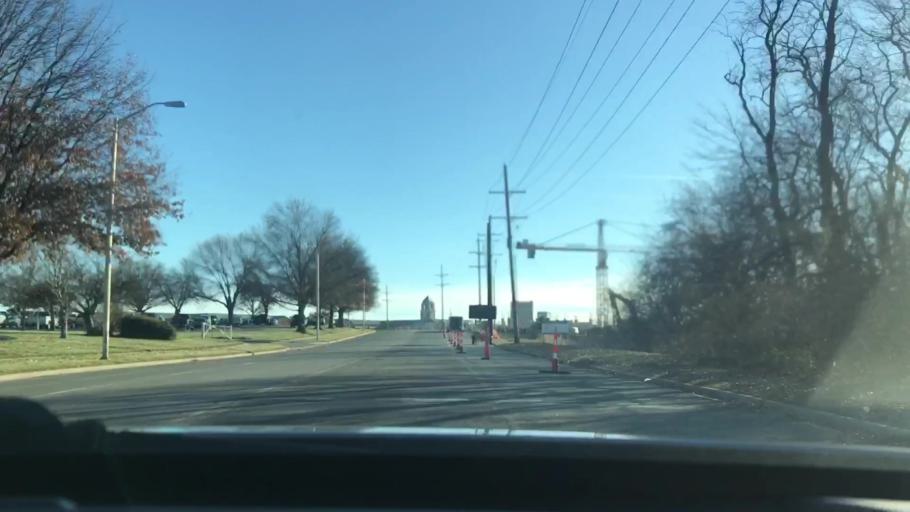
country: US
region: Kansas
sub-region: Johnson County
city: Overland Park
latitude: 38.9250
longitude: -94.6583
